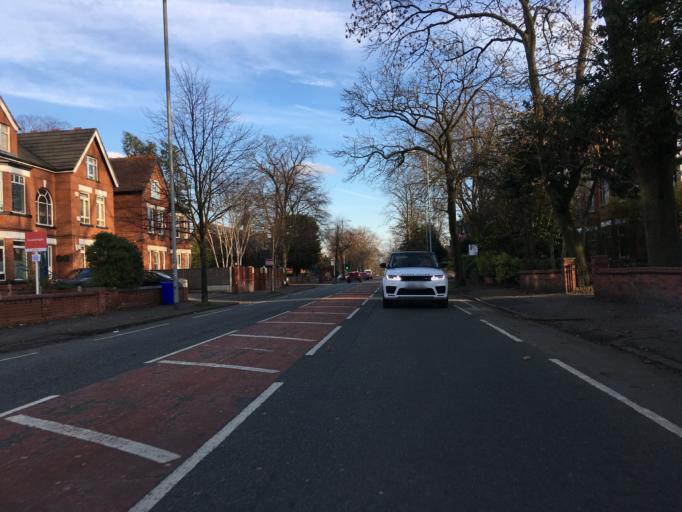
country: GB
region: England
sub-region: Manchester
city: Chorlton cum Hardy
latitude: 53.4427
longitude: -2.2695
